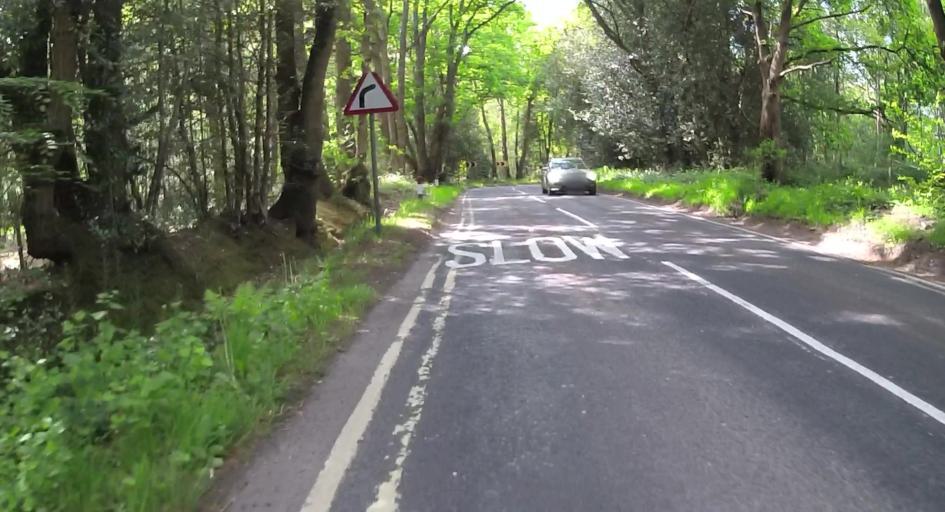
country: GB
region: England
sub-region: Hampshire
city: Fleet
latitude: 51.2886
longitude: -0.7990
